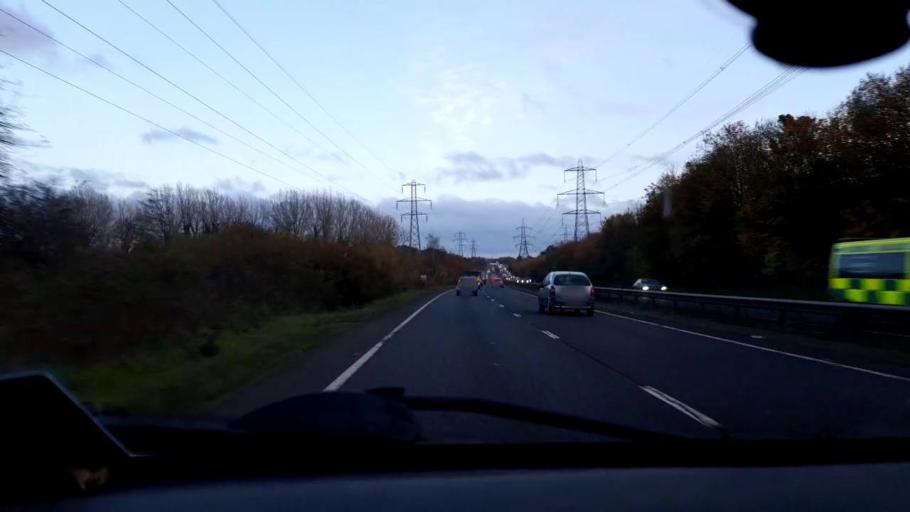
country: GB
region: England
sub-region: Norfolk
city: Cringleford
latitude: 52.5942
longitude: 1.2417
